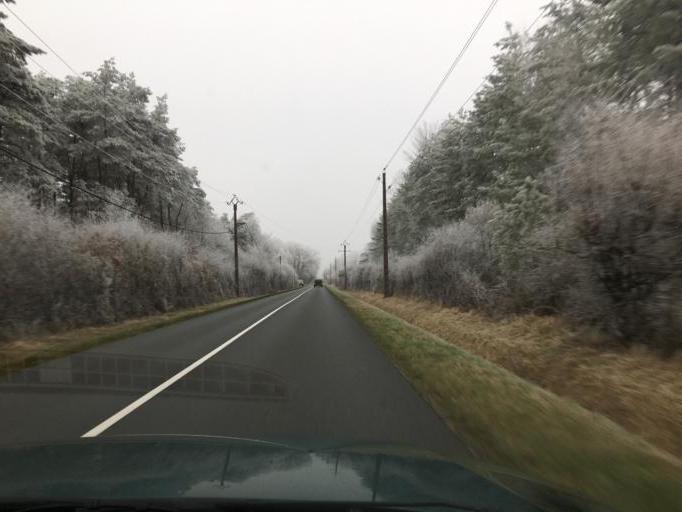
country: FR
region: Centre
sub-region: Departement du Loiret
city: Jouy-le-Potier
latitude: 47.7179
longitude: 1.7977
